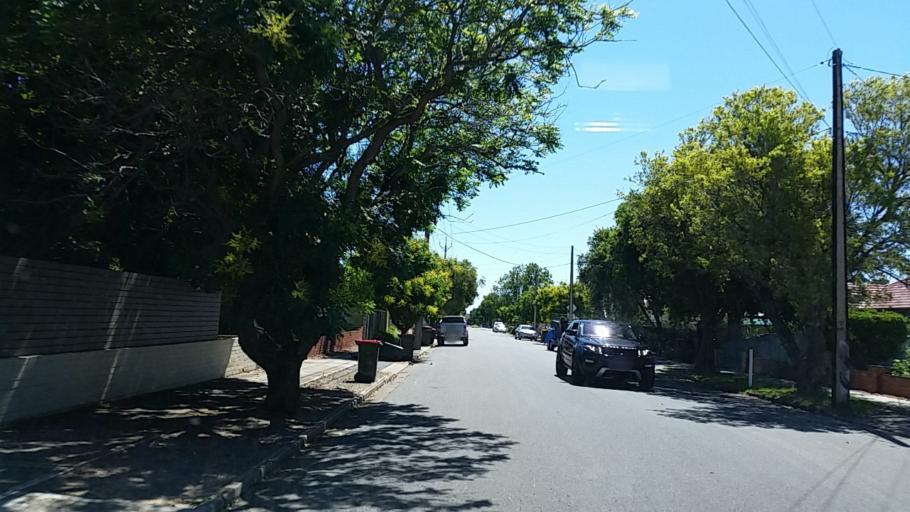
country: AU
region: South Australia
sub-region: Mitcham
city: Clarence Gardens
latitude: -34.9742
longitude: 138.5685
